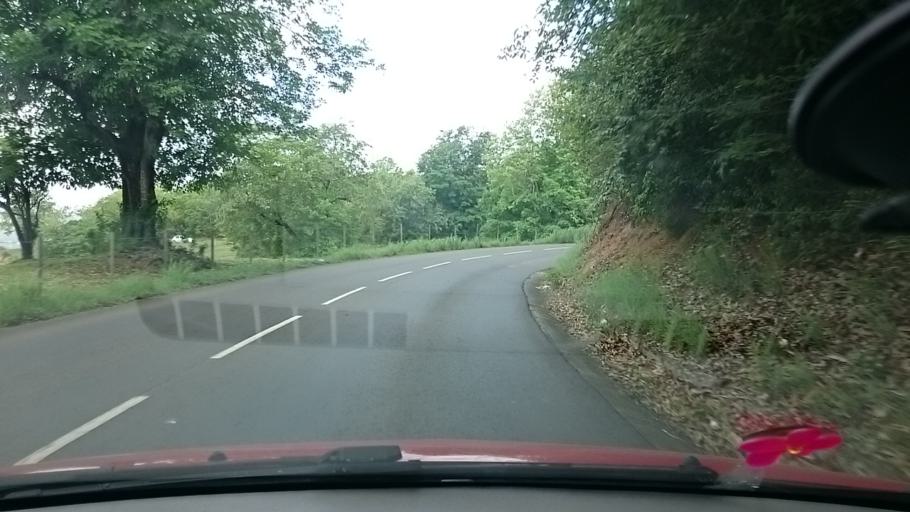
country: MQ
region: Martinique
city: Petite Riviere Salee
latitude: 14.7566
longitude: -60.9277
